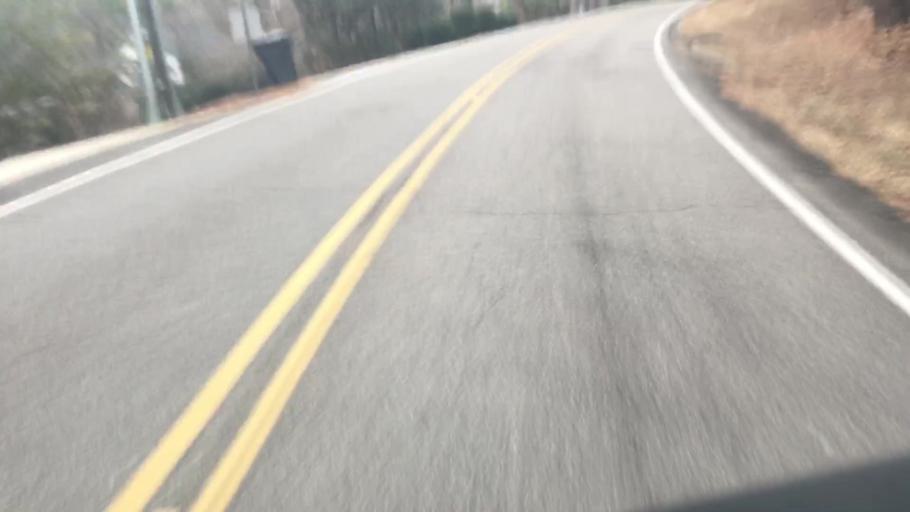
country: US
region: Alabama
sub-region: Jefferson County
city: Vestavia Hills
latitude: 33.4158
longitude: -86.7641
